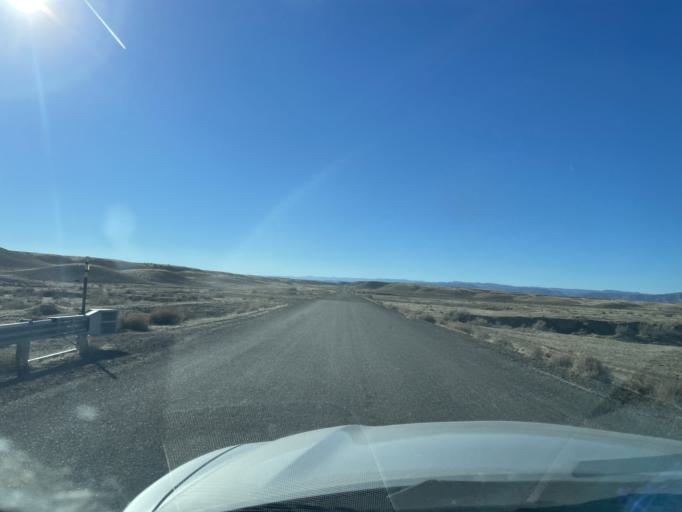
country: US
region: Colorado
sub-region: Mesa County
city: Loma
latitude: 39.2060
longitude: -109.0766
